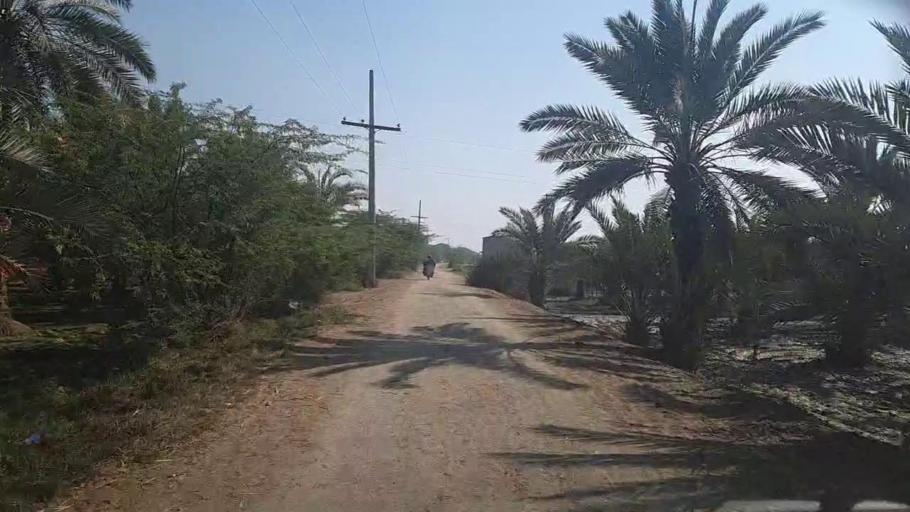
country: PK
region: Sindh
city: Kot Diji
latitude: 27.4381
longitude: 68.7108
